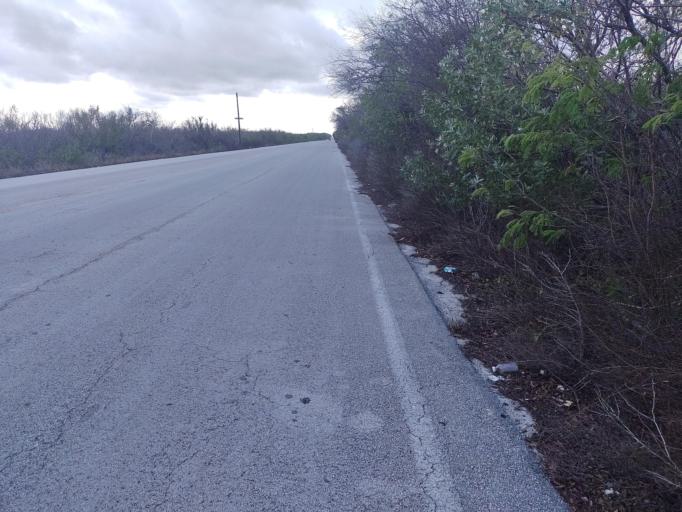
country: MX
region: Quintana Roo
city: San Miguel de Cozumel
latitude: 20.4264
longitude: -86.8463
